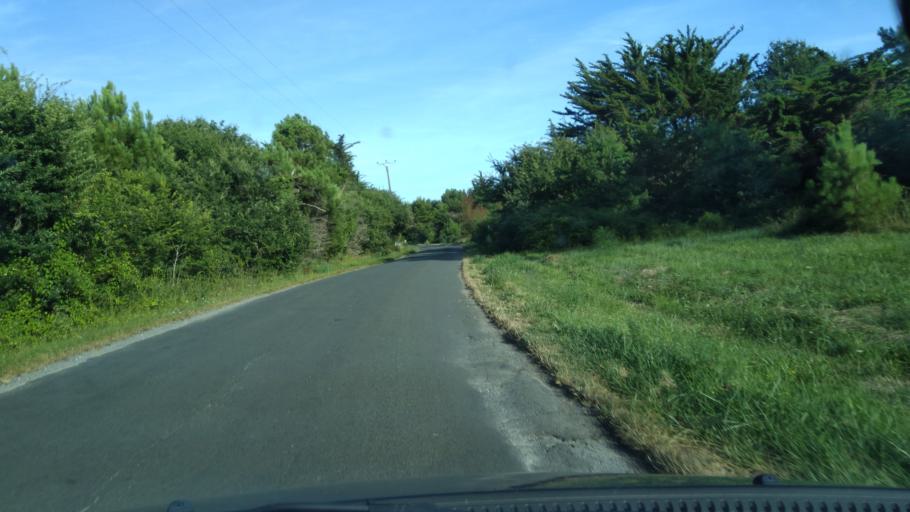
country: FR
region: Poitou-Charentes
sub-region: Departement de la Charente-Maritime
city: Saint-Denis-d'Oleron
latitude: 45.9573
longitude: -1.3602
